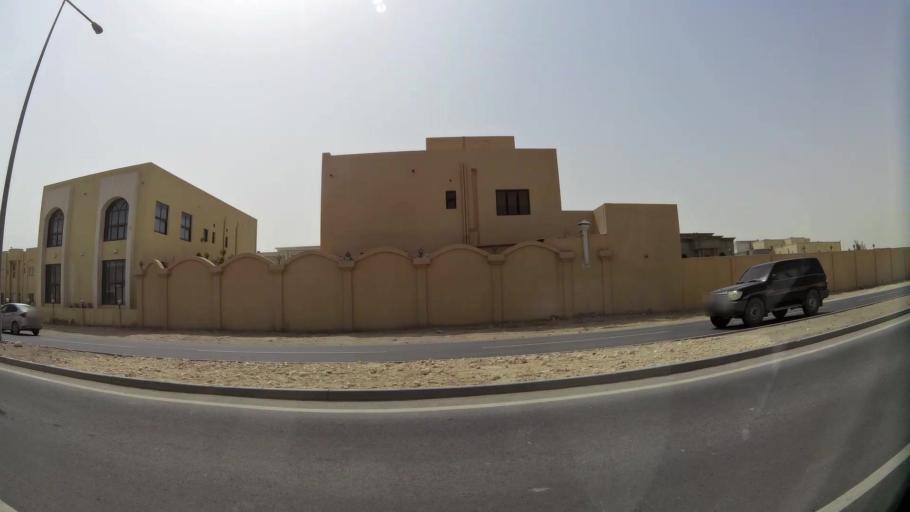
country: QA
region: Baladiyat ar Rayyan
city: Ar Rayyan
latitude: 25.2379
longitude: 51.3817
